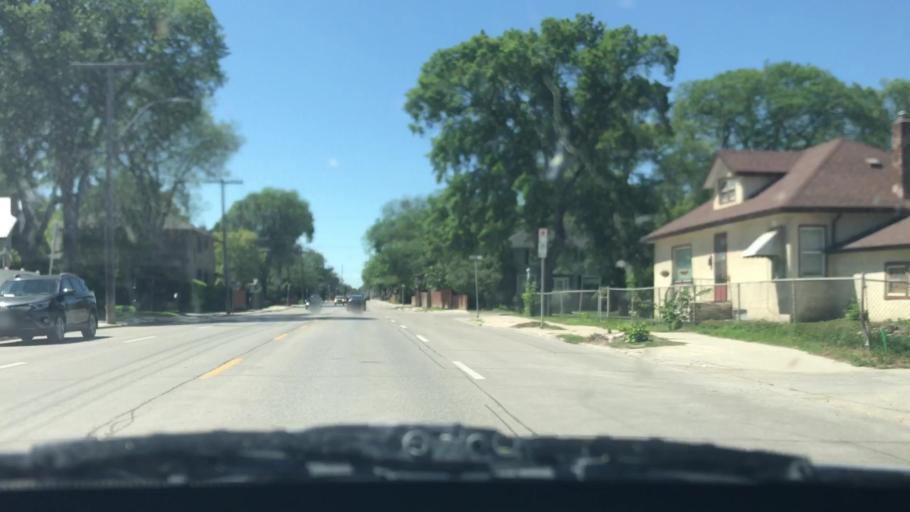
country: CA
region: Manitoba
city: Winnipeg
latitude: 49.8740
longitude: -97.1870
